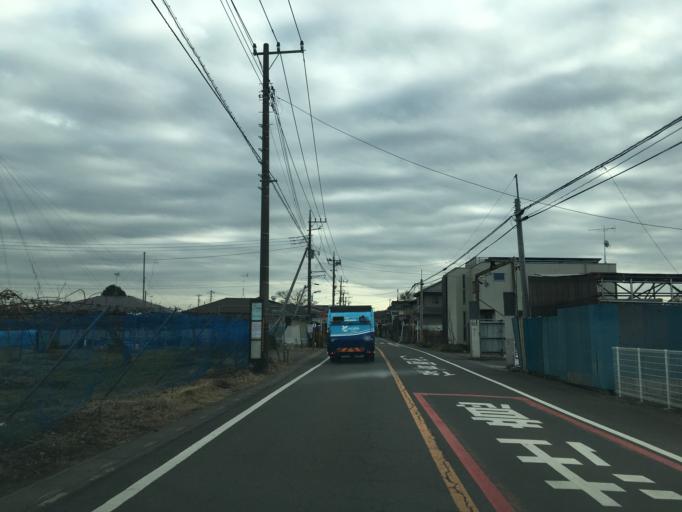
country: JP
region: Saitama
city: Sayama
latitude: 35.7961
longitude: 139.3978
